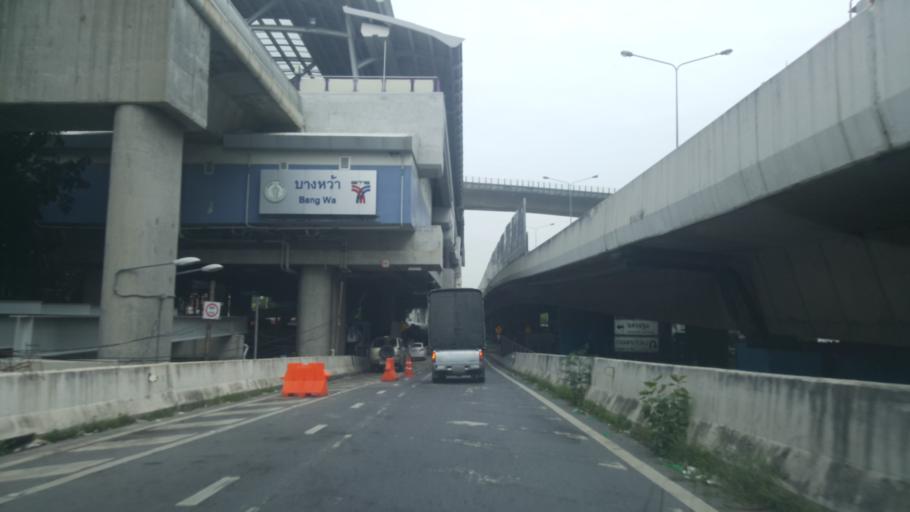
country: TH
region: Bangkok
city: Bangkok Yai
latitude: 13.7198
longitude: 100.4580
